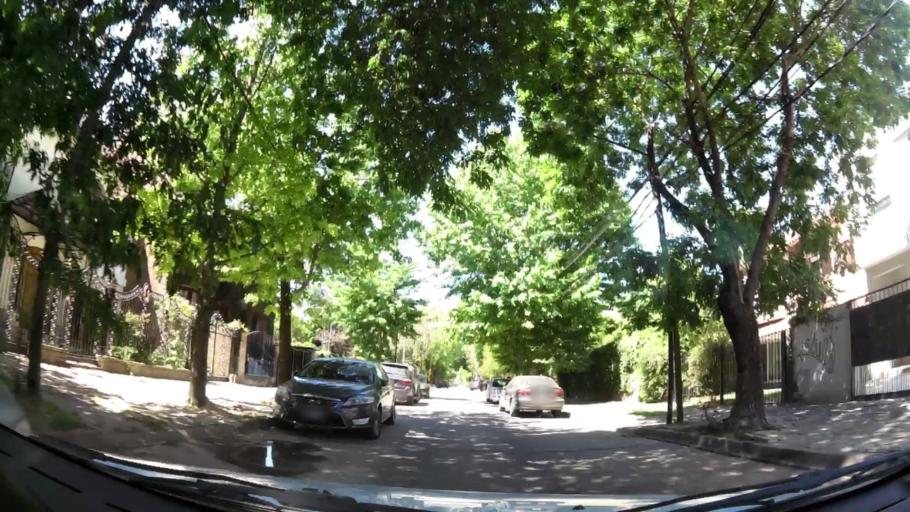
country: AR
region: Buenos Aires
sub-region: Partido de San Isidro
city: San Isidro
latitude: -34.4761
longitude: -58.4952
